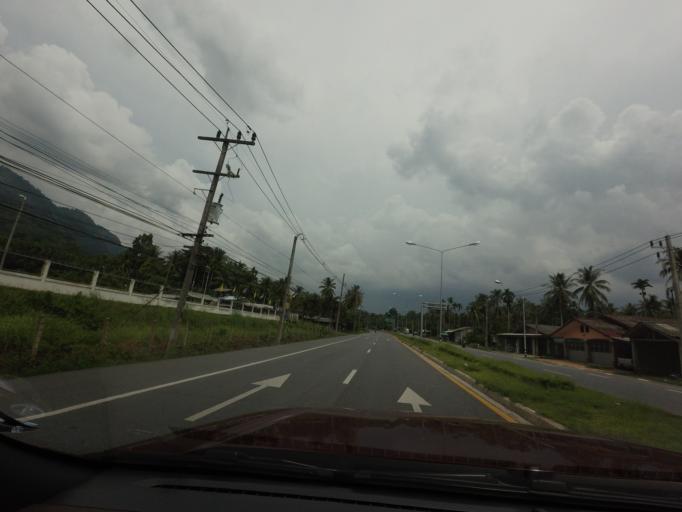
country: TH
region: Yala
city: Krong Pi Nang
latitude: 6.4757
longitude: 101.2657
